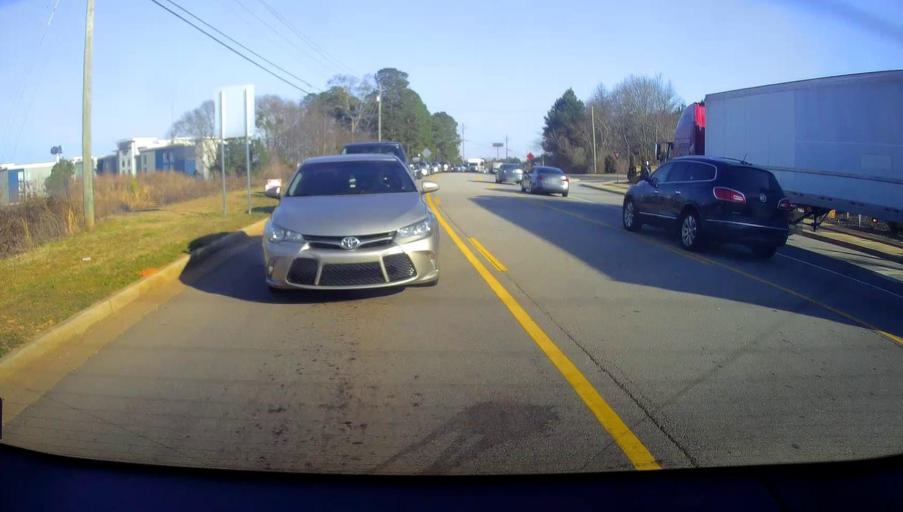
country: US
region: Georgia
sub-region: Henry County
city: McDonough
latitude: 33.4235
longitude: -84.1818
